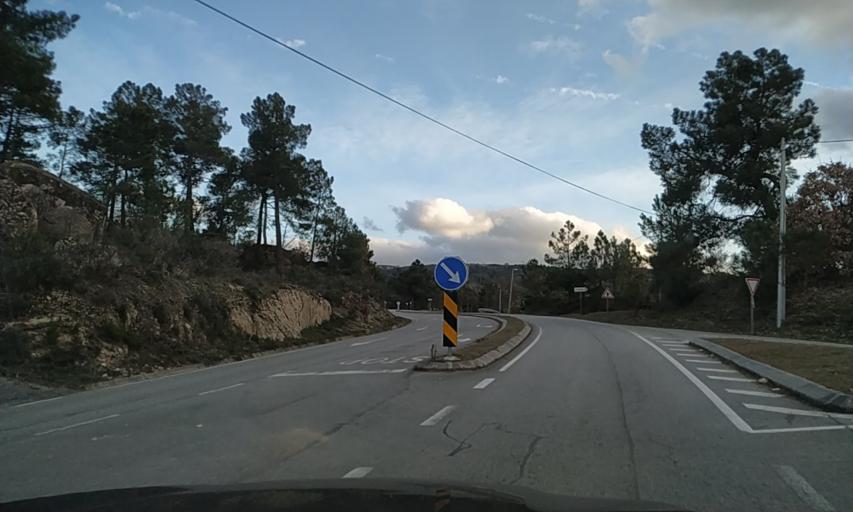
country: PT
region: Braganca
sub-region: Carrazeda de Ansiaes
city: Carrazeda de Anciaes
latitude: 41.2633
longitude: -7.3249
